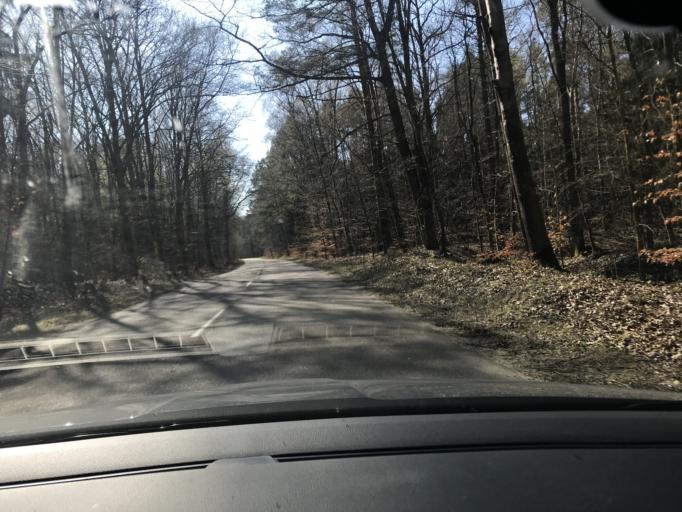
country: PL
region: Pomeranian Voivodeship
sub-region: Powiat nowodworski
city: Krynica Morska
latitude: 54.3601
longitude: 19.3458
